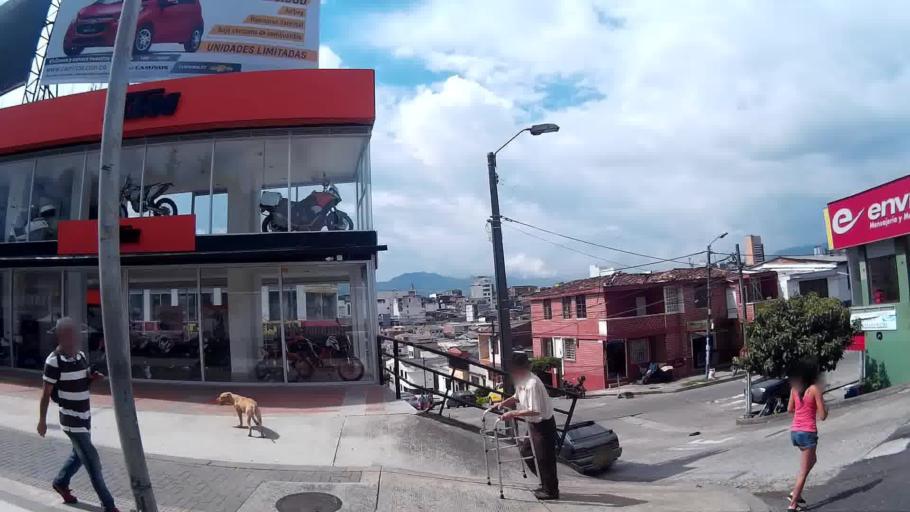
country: CO
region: Risaralda
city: Pereira
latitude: 4.8118
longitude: -75.7048
